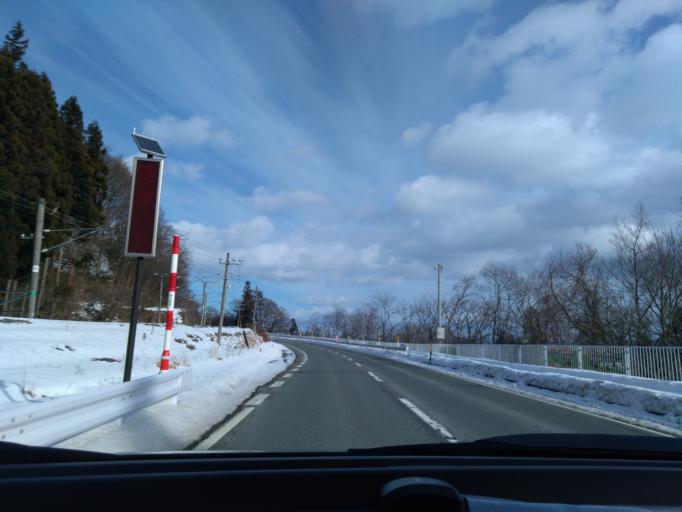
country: JP
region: Iwate
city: Shizukuishi
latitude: 39.6885
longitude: 140.9209
